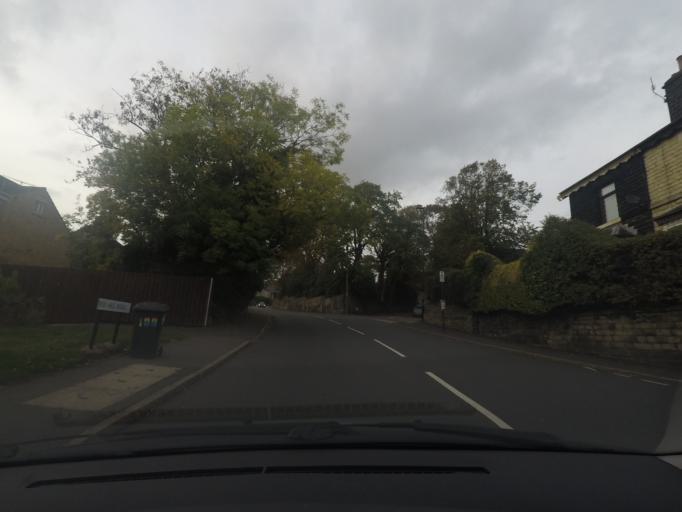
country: GB
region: England
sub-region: Sheffield
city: Oughtibridge
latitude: 53.4231
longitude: -1.4991
